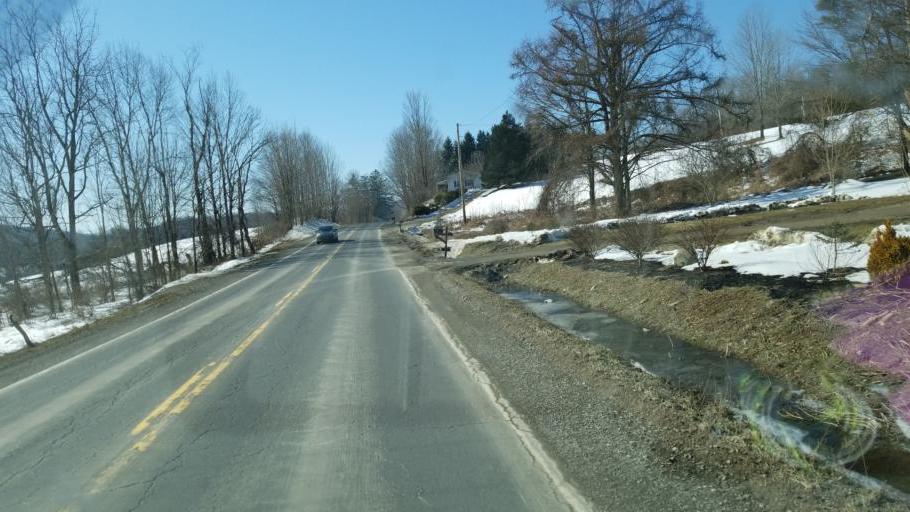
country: US
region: New York
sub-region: Steuben County
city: Hornell
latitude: 42.3594
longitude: -77.7013
